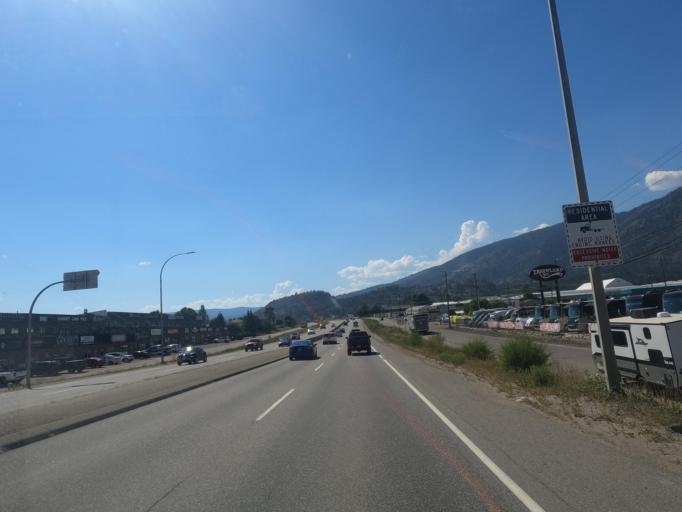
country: CA
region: British Columbia
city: West Kelowna
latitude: 49.8627
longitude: -119.5775
